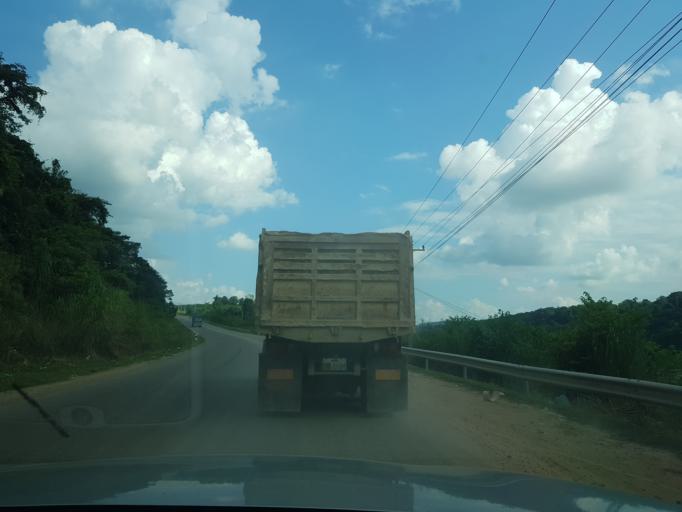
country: TH
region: Nong Khai
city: Sangkhom
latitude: 18.0394
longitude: 102.3584
